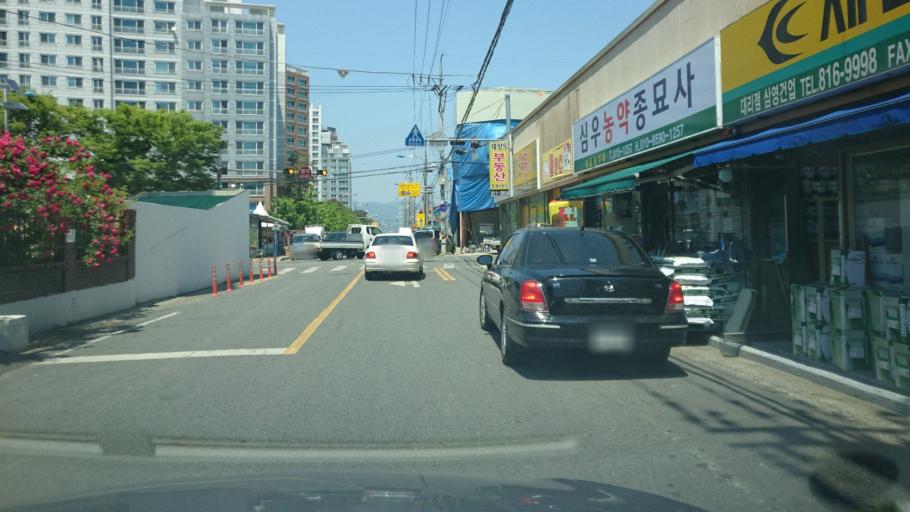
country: KR
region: Gyeongsangbuk-do
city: Gyeongsan-si
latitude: 35.8298
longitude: 128.7388
